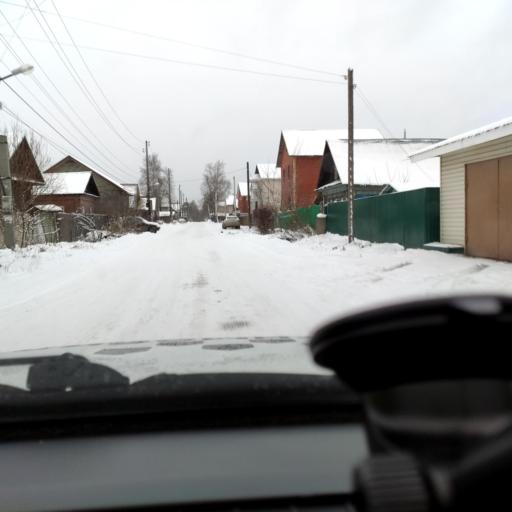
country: RU
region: Perm
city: Perm
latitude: 58.0591
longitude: 56.3639
